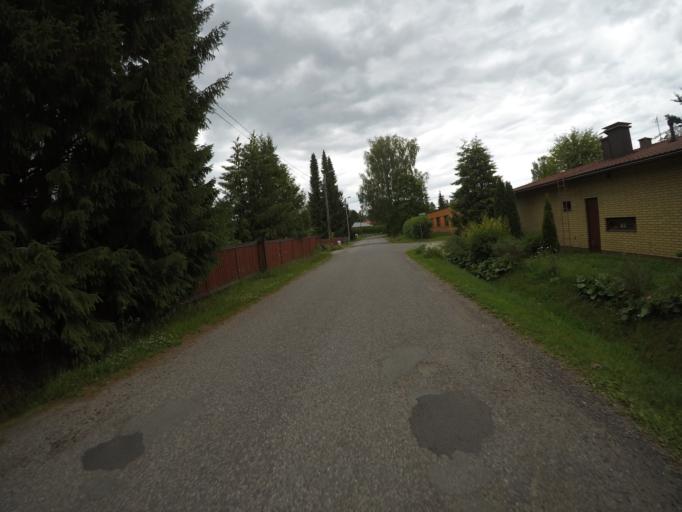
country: FI
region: Haeme
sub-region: Haemeenlinna
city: Haemeenlinna
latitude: 60.9814
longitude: 24.4444
